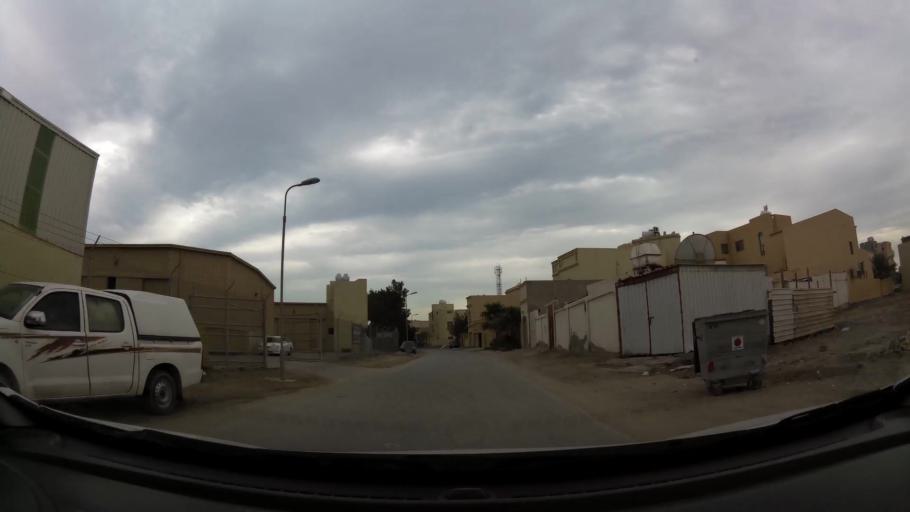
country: BH
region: Northern
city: Sitrah
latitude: 26.1720
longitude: 50.6047
